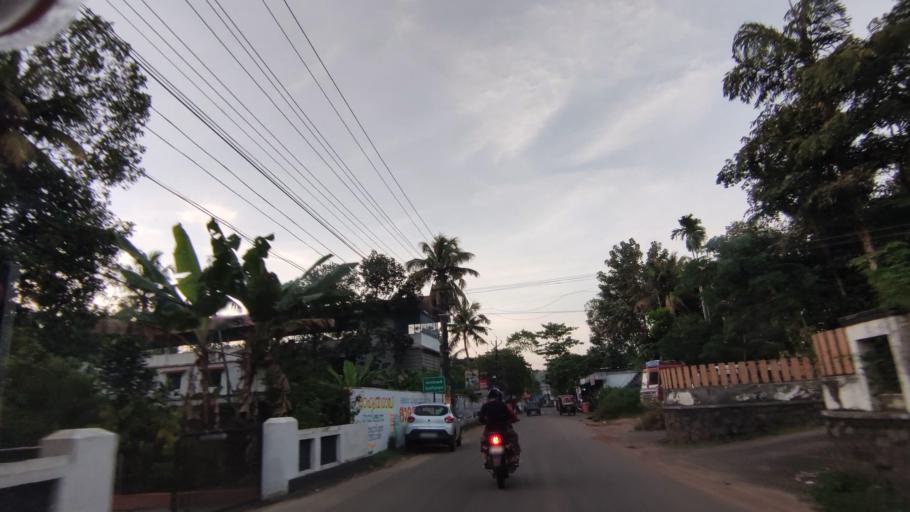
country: IN
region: Kerala
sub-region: Kottayam
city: Kottayam
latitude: 9.6546
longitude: 76.5065
